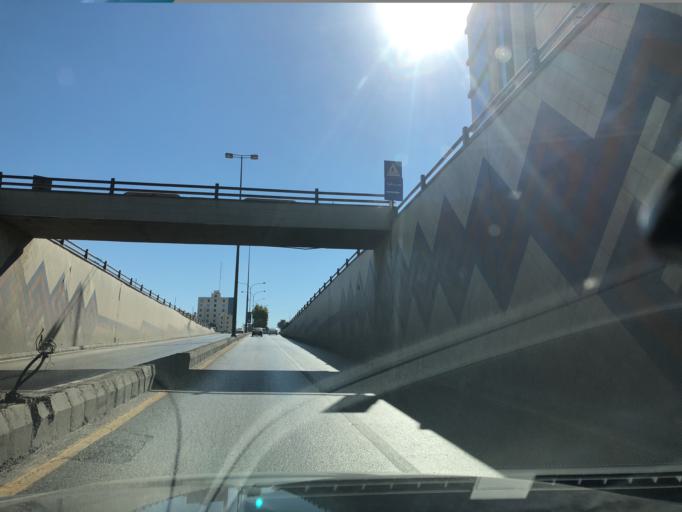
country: JO
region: Amman
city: Al Jubayhah
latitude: 31.9745
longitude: 35.8658
